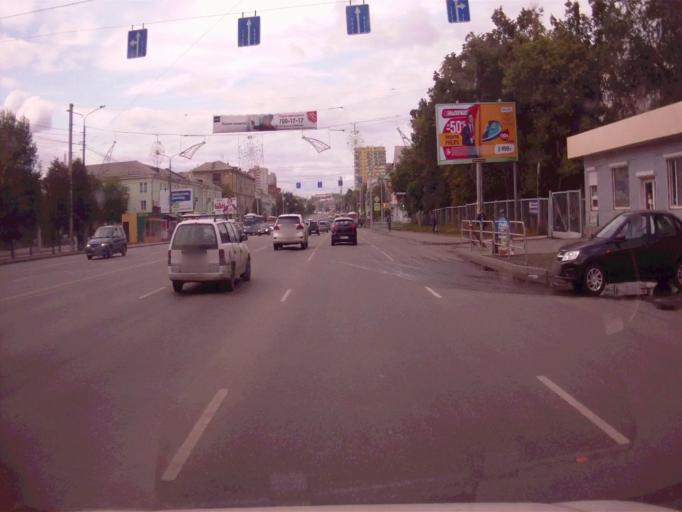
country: RU
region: Chelyabinsk
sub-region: Gorod Chelyabinsk
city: Chelyabinsk
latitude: 55.1410
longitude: 61.3948
